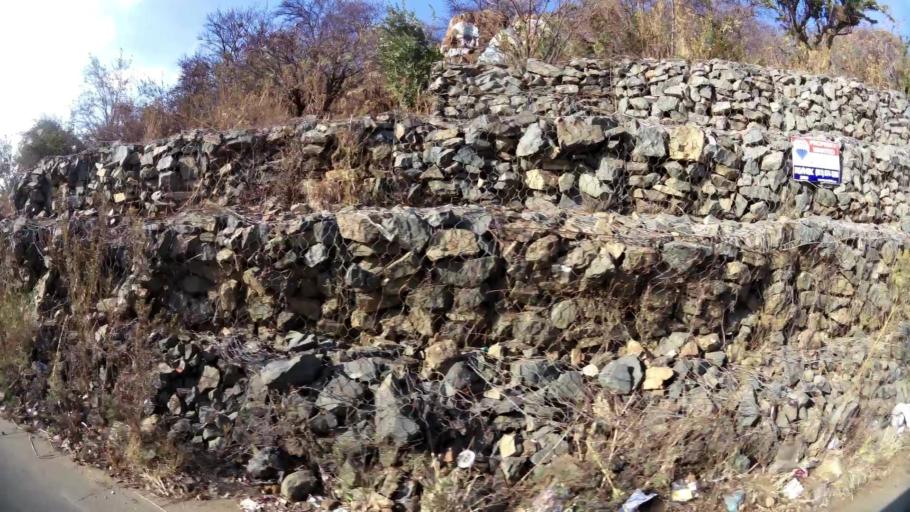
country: ZA
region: Gauteng
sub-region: City of Johannesburg Metropolitan Municipality
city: Soweto
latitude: -26.2629
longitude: 27.9169
